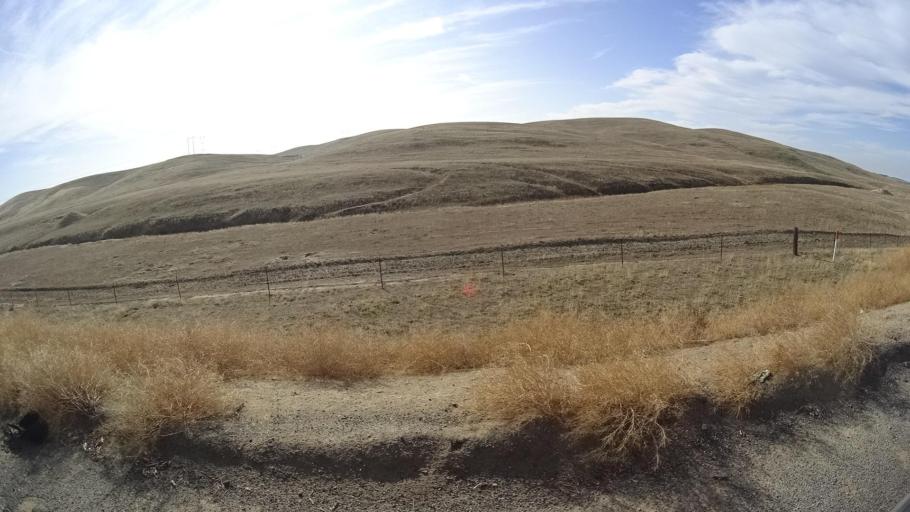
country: US
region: California
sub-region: Tulare County
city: Richgrove
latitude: 35.6196
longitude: -119.0423
